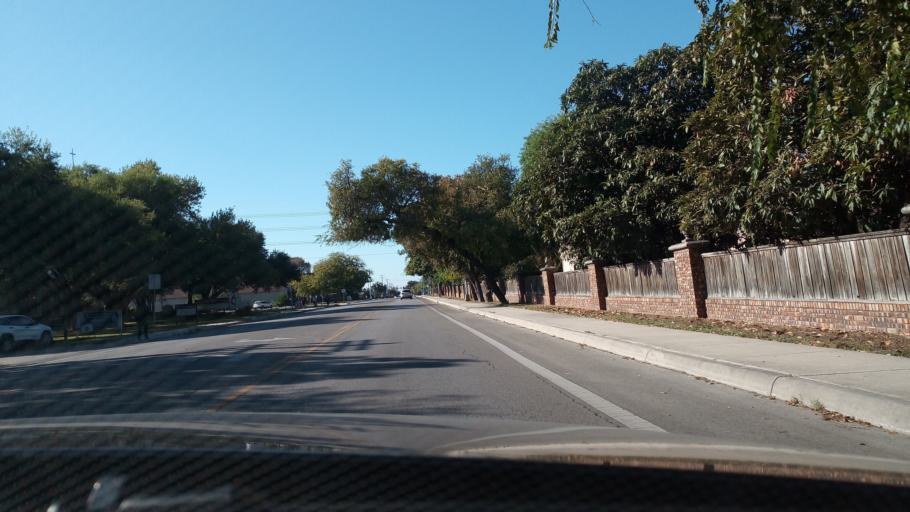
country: US
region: Texas
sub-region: Bexar County
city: Alamo Heights
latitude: 29.5305
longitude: -98.4451
